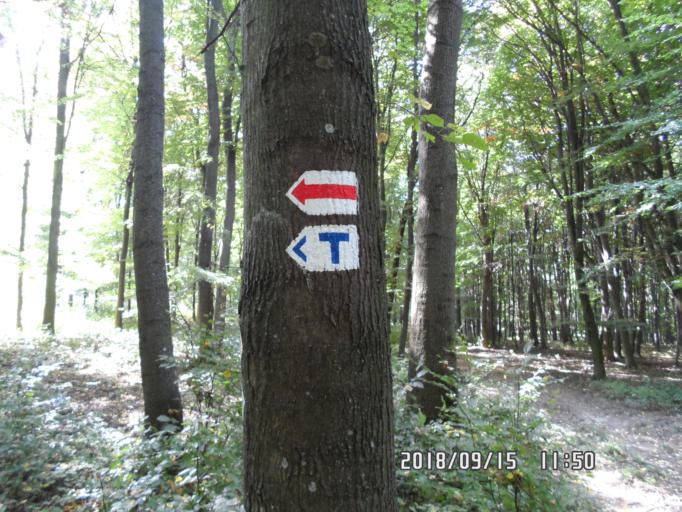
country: HU
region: Veszprem
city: Cseteny
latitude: 47.2514
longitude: 17.9767
